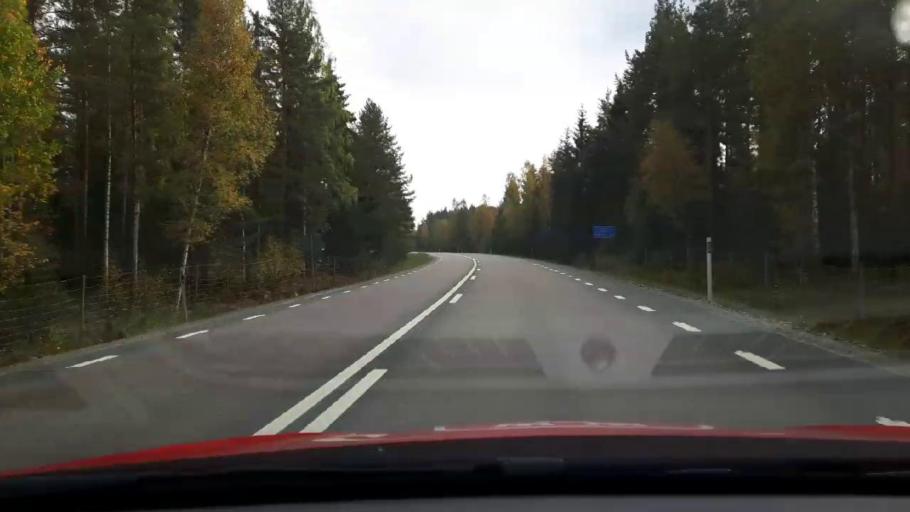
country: SE
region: Gaevleborg
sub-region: Bollnas Kommun
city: Kilafors
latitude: 61.2740
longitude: 16.5283
